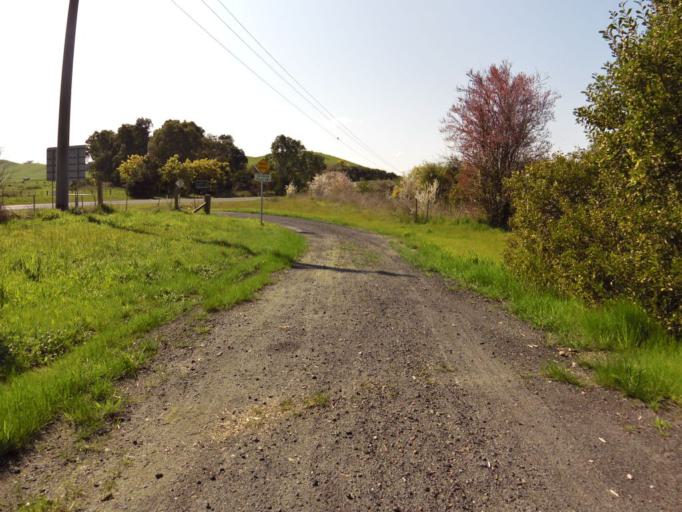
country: AU
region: Victoria
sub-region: Murrindindi
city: Alexandra
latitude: -37.1496
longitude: 145.5856
